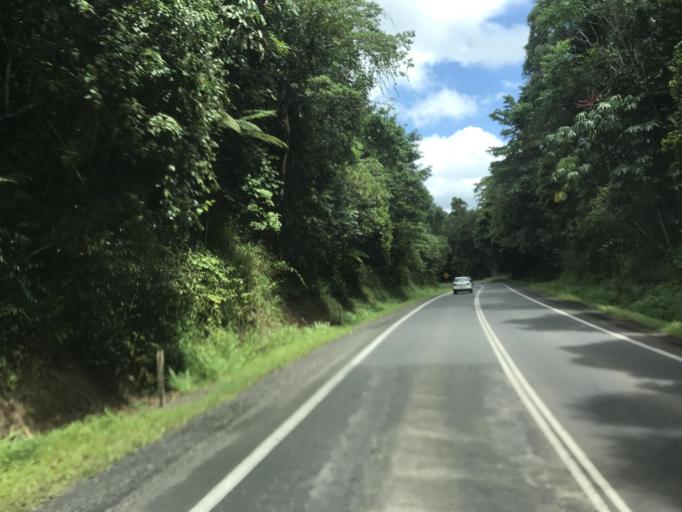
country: AU
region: Queensland
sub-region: Tablelands
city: Ravenshoe
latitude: -17.6022
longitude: 145.7588
